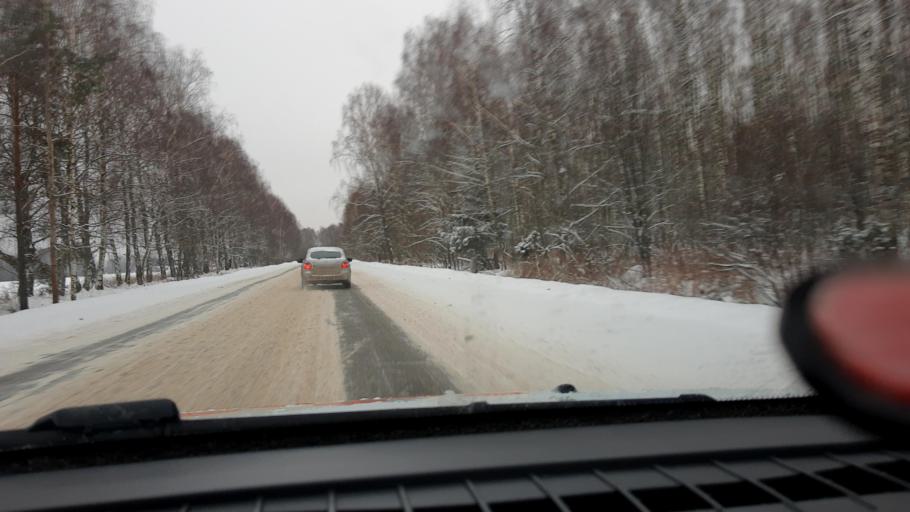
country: RU
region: Nizjnij Novgorod
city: Pamyat' Parizhskoy Kommuny
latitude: 56.2538
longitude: 44.4708
